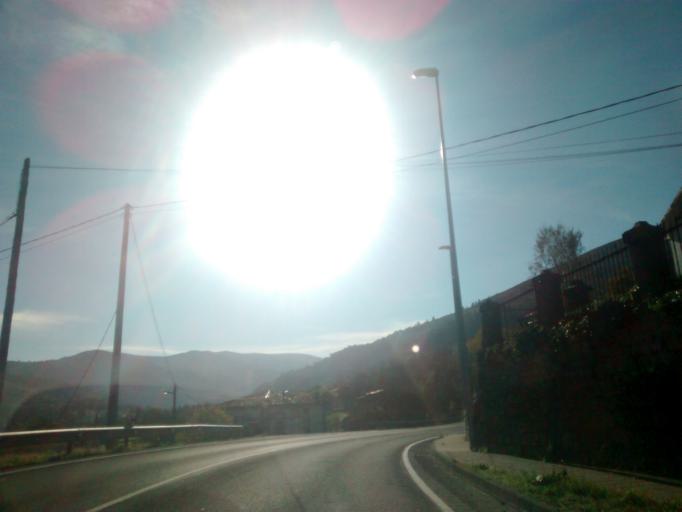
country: ES
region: Cantabria
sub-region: Provincia de Cantabria
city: Santiurde de Toranzo
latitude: 43.1902
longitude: -3.9130
